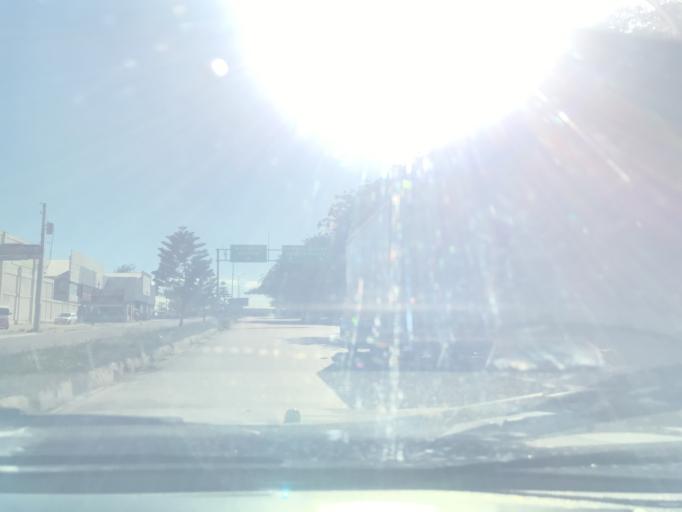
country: DO
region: Santiago
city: Santiago de los Caballeros
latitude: 19.4255
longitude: -70.6798
